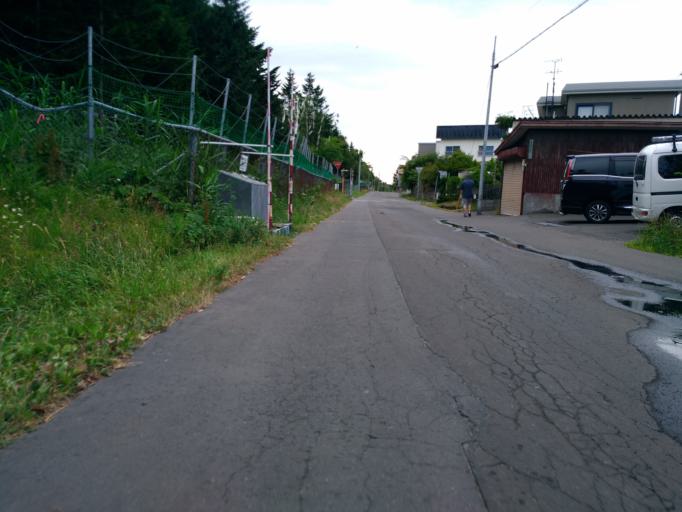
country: JP
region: Hokkaido
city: Ebetsu
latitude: 43.0823
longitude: 141.5255
